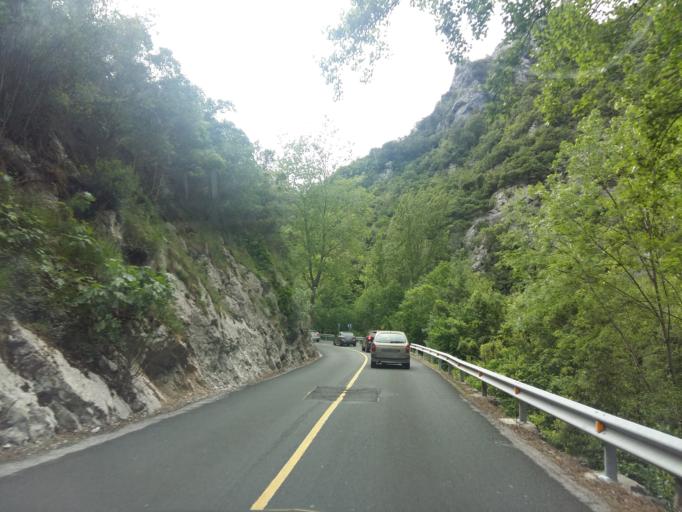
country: ES
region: Cantabria
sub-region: Provincia de Cantabria
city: Tresviso
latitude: 43.2479
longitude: -4.5914
